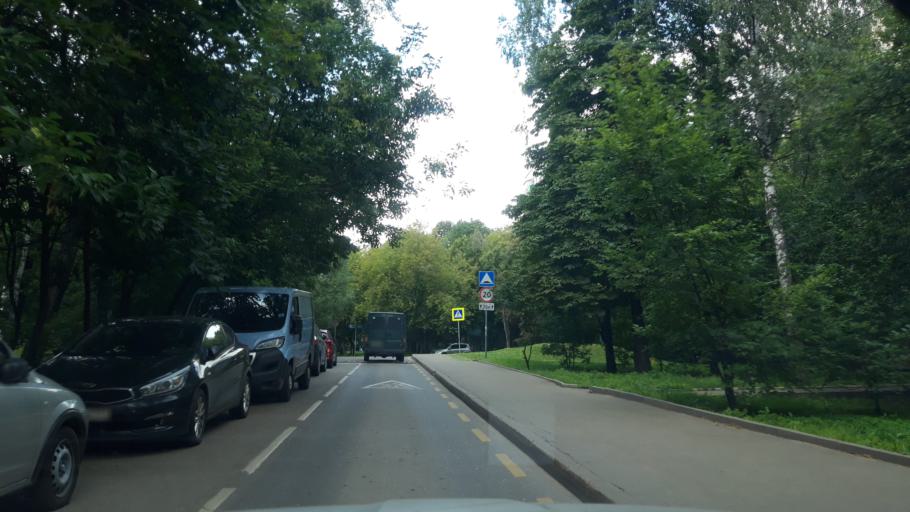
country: RU
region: Moskovskaya
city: Levoberezhnyy
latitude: 55.8454
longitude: 37.4826
